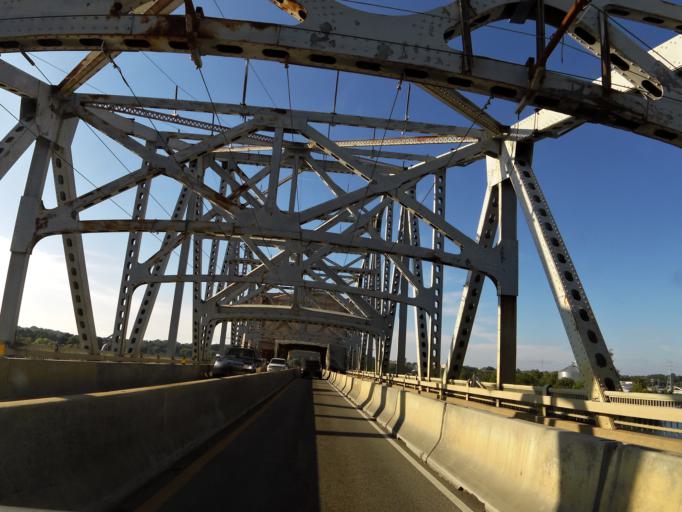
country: US
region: Alabama
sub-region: Lauderdale County
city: Florence
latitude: 34.7832
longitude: -87.6714
